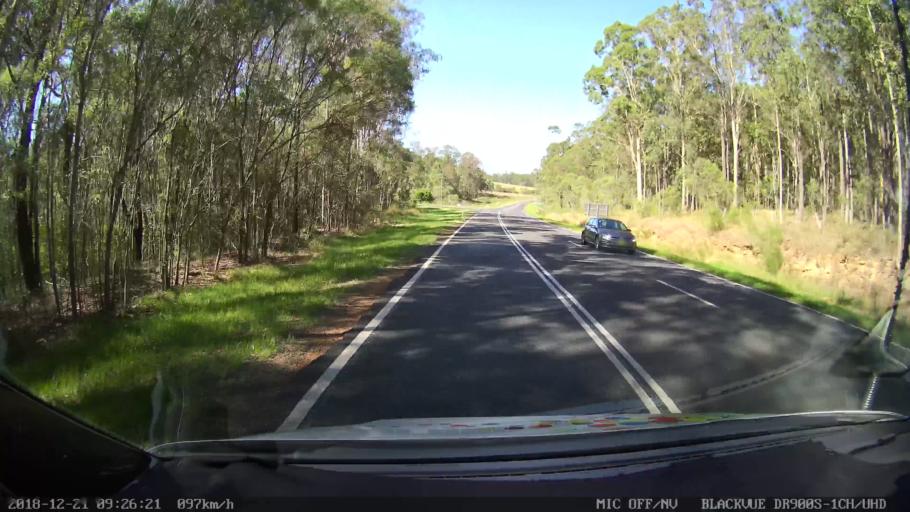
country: AU
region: New South Wales
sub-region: Clarence Valley
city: Maclean
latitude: -29.3920
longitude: 153.0032
